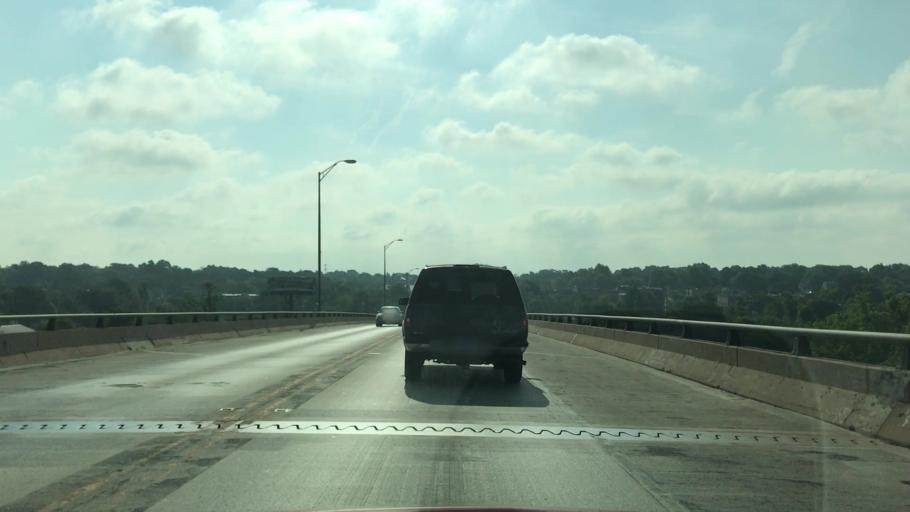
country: US
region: Illinois
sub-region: Will County
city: Lockport
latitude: 41.5908
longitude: -88.0642
